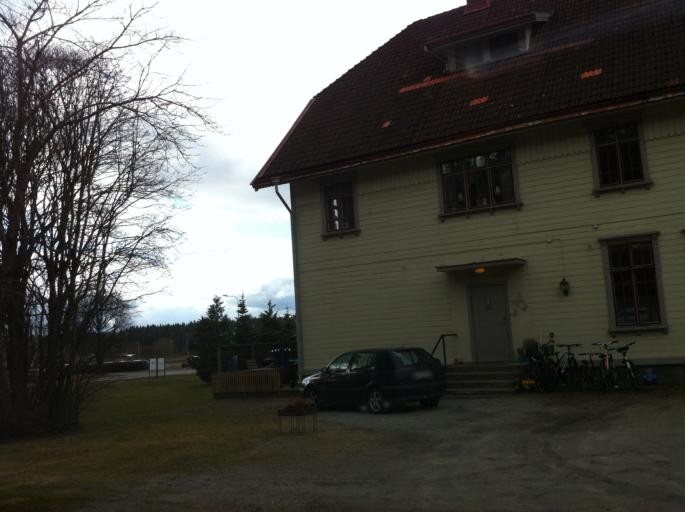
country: SE
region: Vaestra Goetaland
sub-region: Tranemo Kommun
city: Tranemo
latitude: 57.4772
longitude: 13.3429
